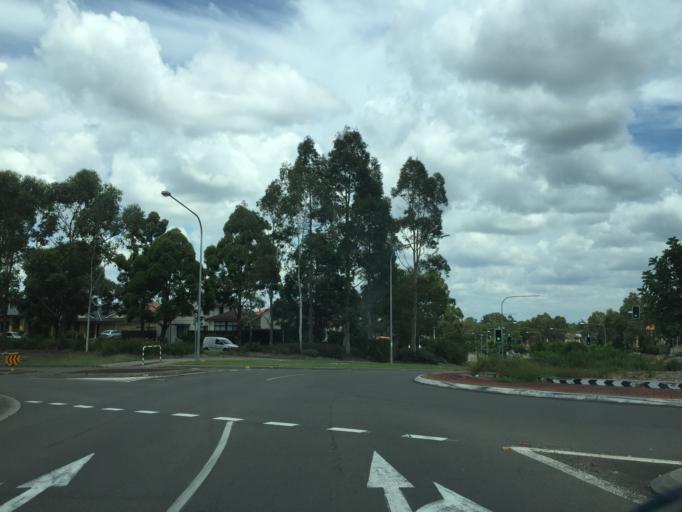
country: AU
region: New South Wales
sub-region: The Hills Shire
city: Beaumont Hills
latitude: -33.7034
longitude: 150.9471
